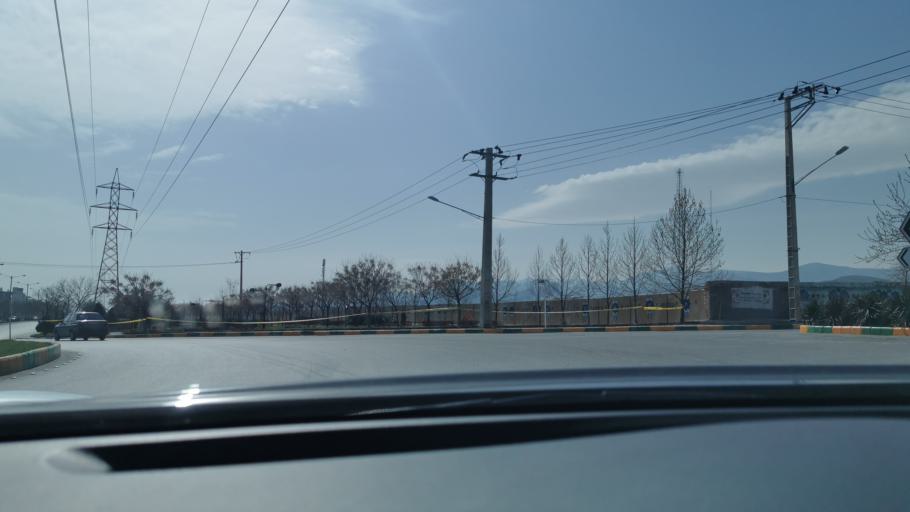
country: IR
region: Razavi Khorasan
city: Mashhad
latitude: 36.2882
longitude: 59.5342
